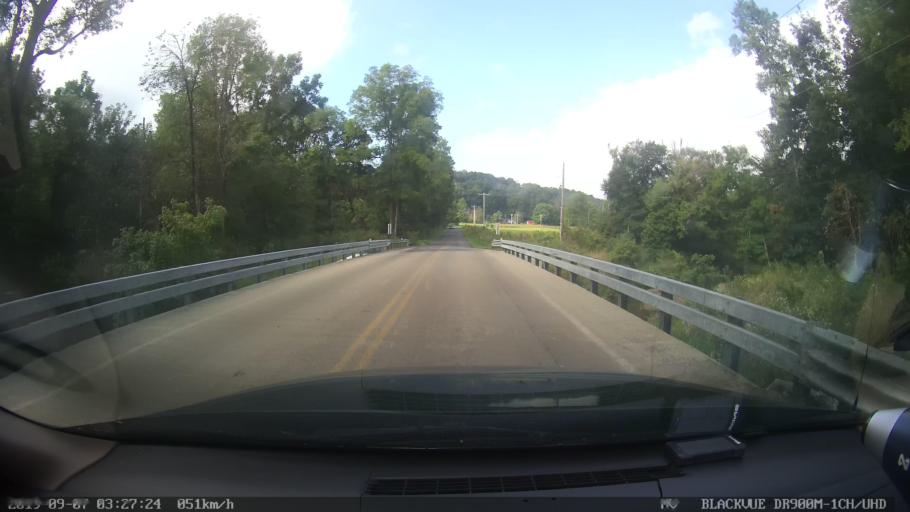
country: US
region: Ohio
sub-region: Licking County
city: Granville
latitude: 40.1233
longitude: -82.5031
